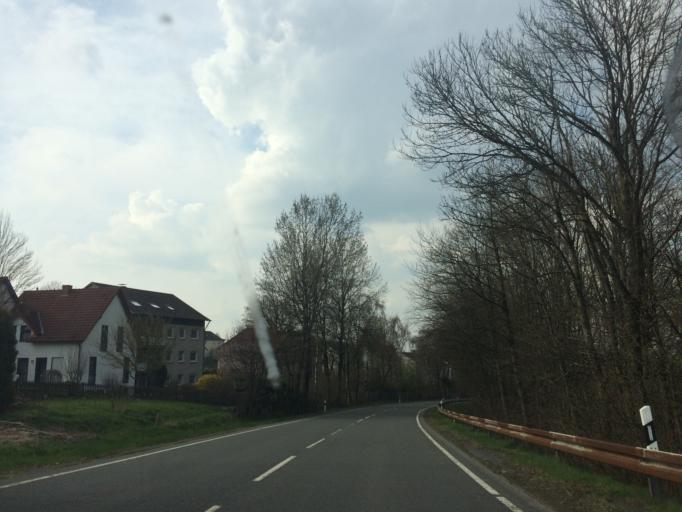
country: DE
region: North Rhine-Westphalia
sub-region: Regierungsbezirk Arnsberg
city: Nachrodt-Wiblingwerde
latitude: 51.3079
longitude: 7.6200
